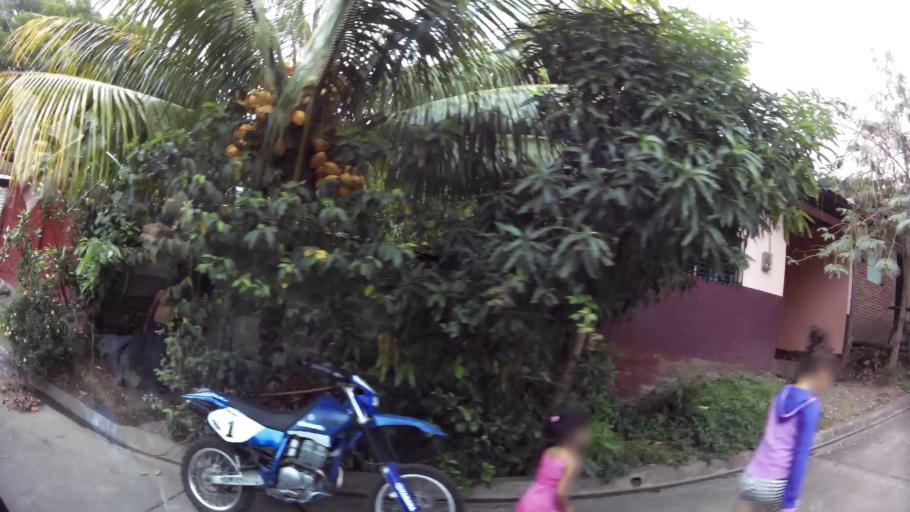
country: NI
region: Matagalpa
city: Matagalpa
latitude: 12.9183
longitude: -85.9189
